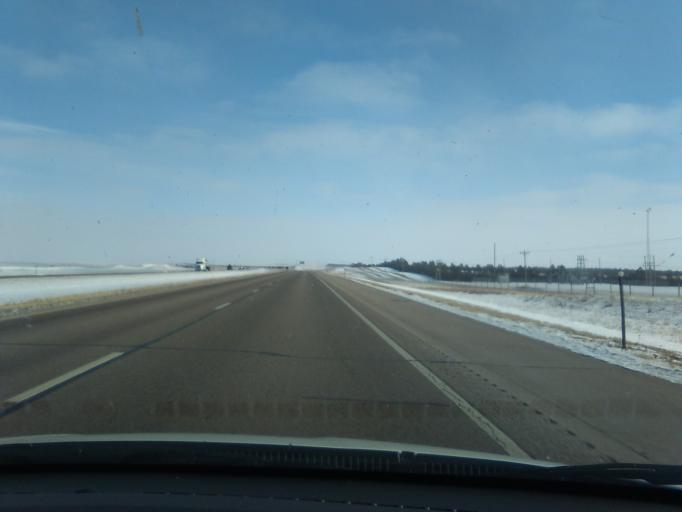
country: US
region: Nebraska
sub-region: Kimball County
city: Kimball
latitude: 41.1919
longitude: -103.7811
